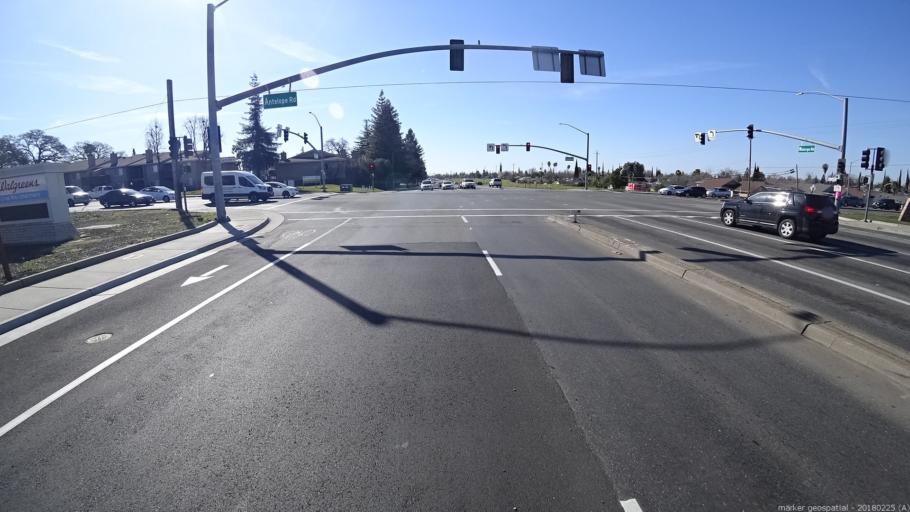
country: US
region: California
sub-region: Sacramento County
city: North Highlands
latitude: 38.7042
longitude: -121.3635
